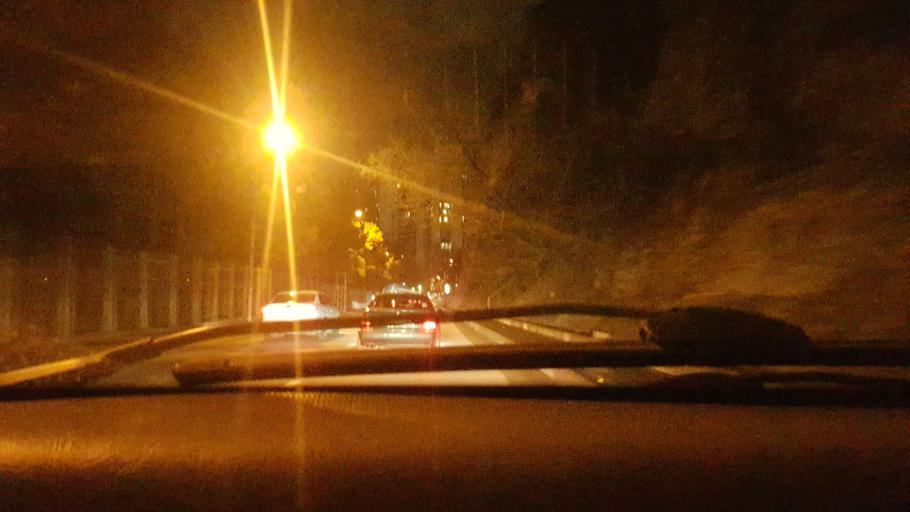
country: GE
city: Tsqnet'i
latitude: 41.7214
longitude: 44.7550
